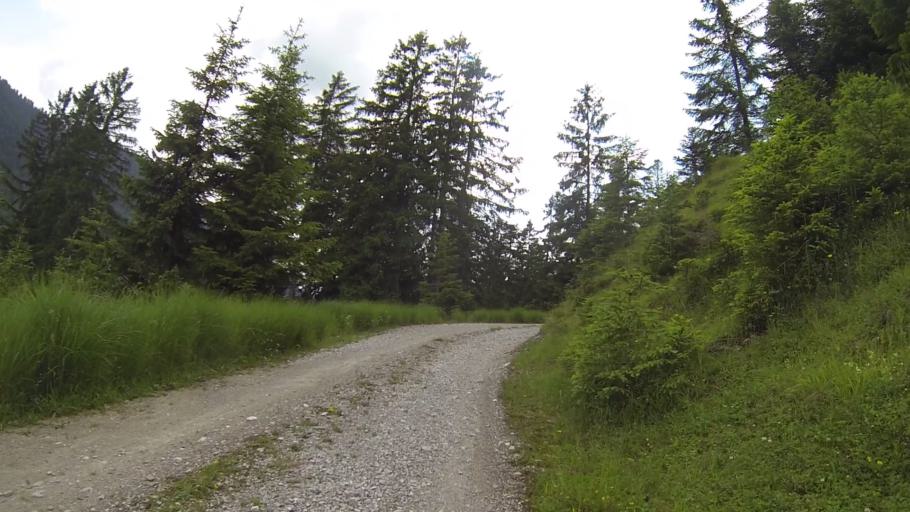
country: AT
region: Tyrol
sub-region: Politischer Bezirk Reutte
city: Breitenwang
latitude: 47.5023
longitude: 10.7816
